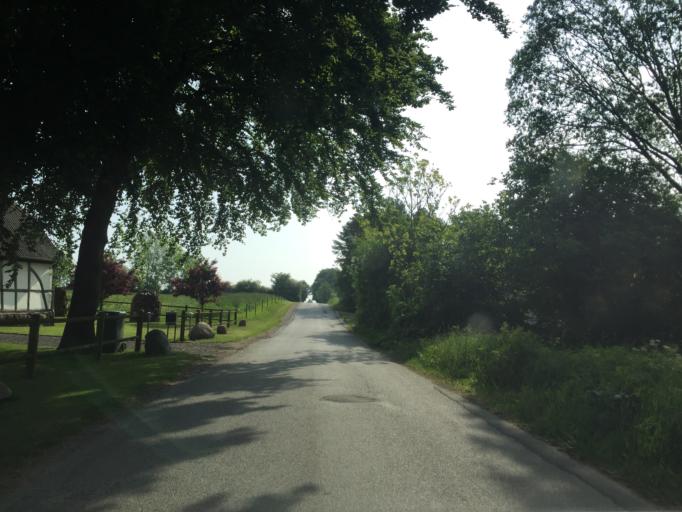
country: DK
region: South Denmark
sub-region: Svendborg Kommune
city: Thuro By
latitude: 55.1241
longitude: 10.7511
